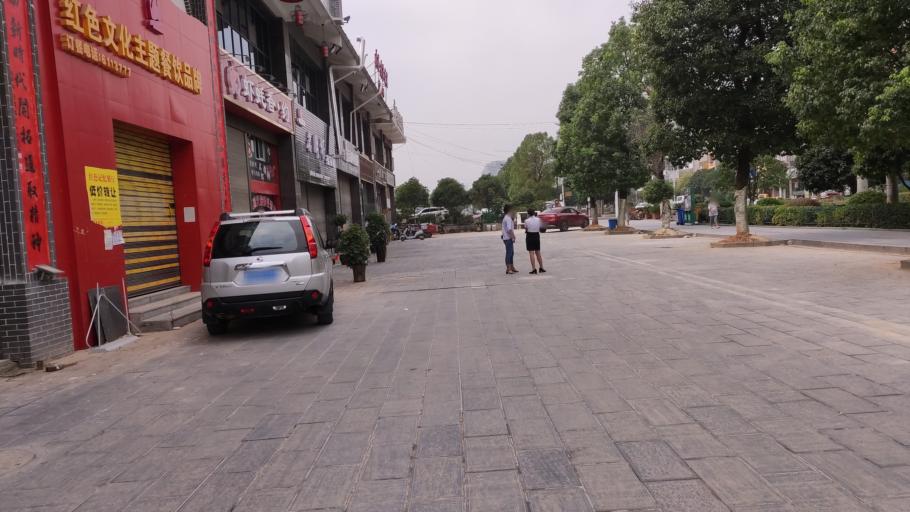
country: CN
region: Guizhou Sheng
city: Zhongchao
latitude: 26.2285
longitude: 109.1342
